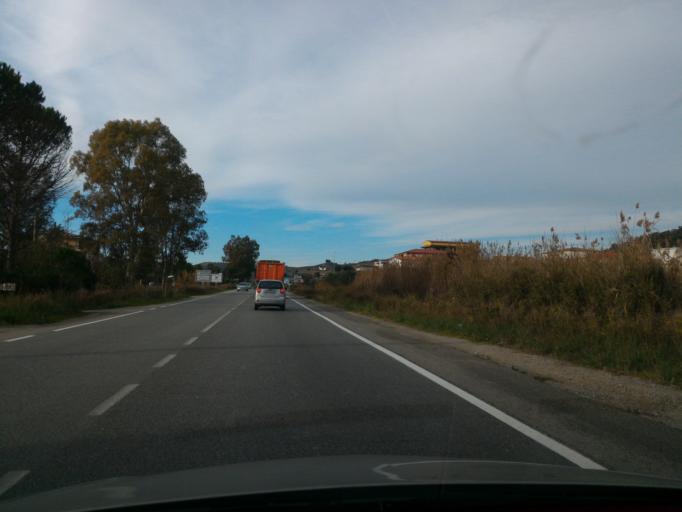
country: IT
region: Calabria
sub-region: Provincia di Crotone
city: Crotone
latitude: 39.0580
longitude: 17.0925
